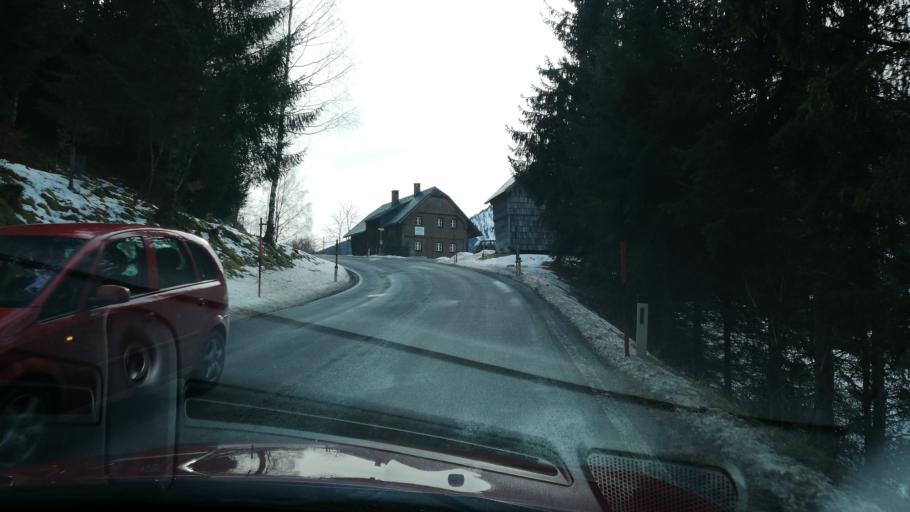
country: AT
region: Styria
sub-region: Politischer Bezirk Liezen
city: Donnersbach
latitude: 47.4515
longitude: 14.1423
